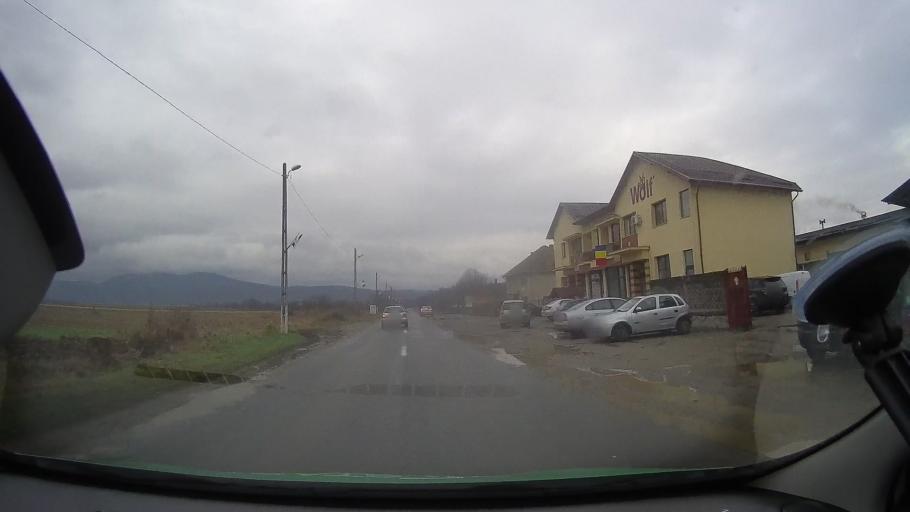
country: RO
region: Arad
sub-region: Comuna Buteni
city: Buteni
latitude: 46.3354
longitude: 22.1266
